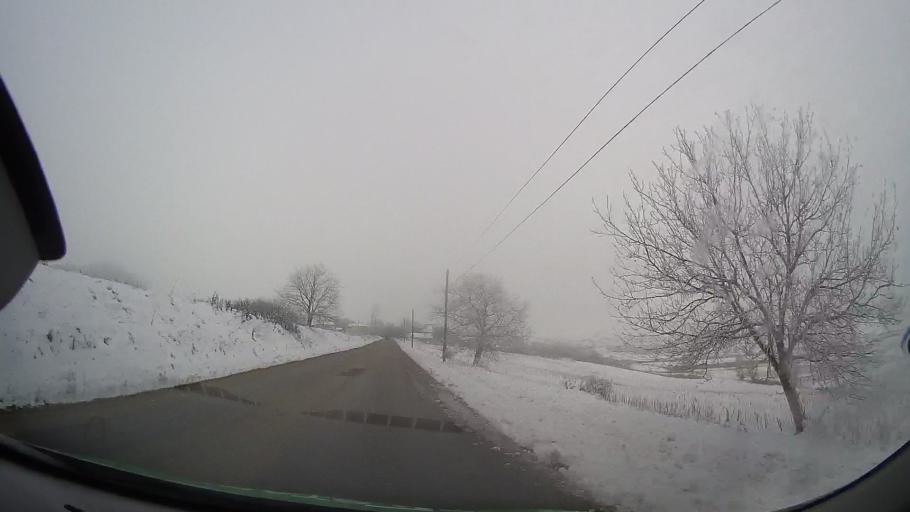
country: RO
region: Bacau
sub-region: Comuna Stanisesti
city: Stanisesti
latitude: 46.4095
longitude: 27.2712
